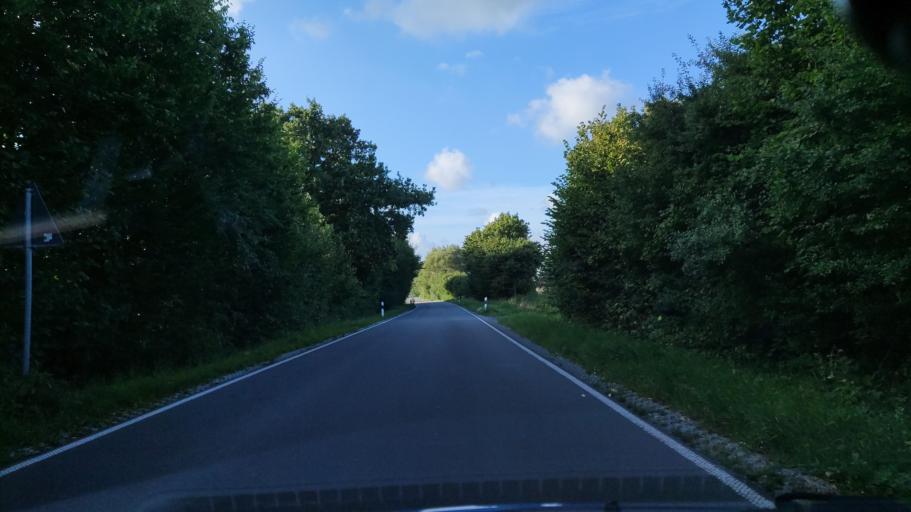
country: DE
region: Schleswig-Holstein
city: Glasau
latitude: 54.0809
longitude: 10.4986
